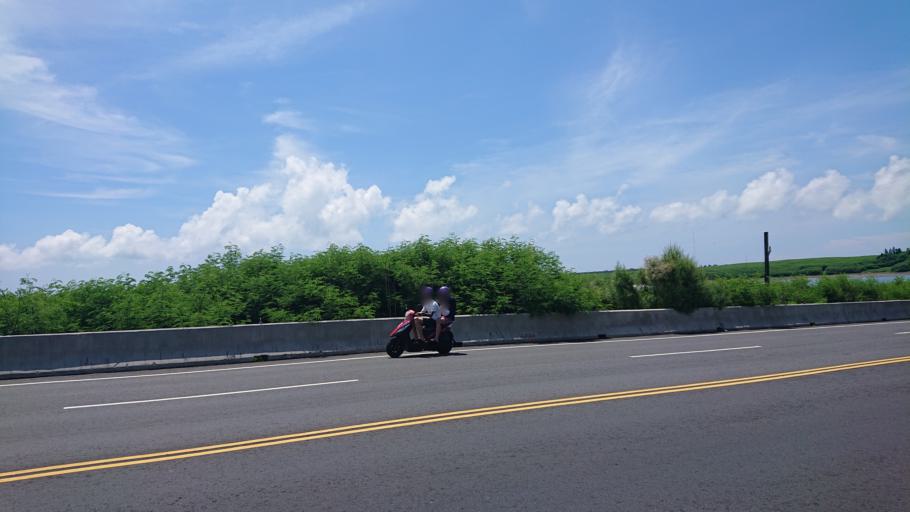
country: TW
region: Taiwan
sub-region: Penghu
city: Ma-kung
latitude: 23.6189
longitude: 119.6057
